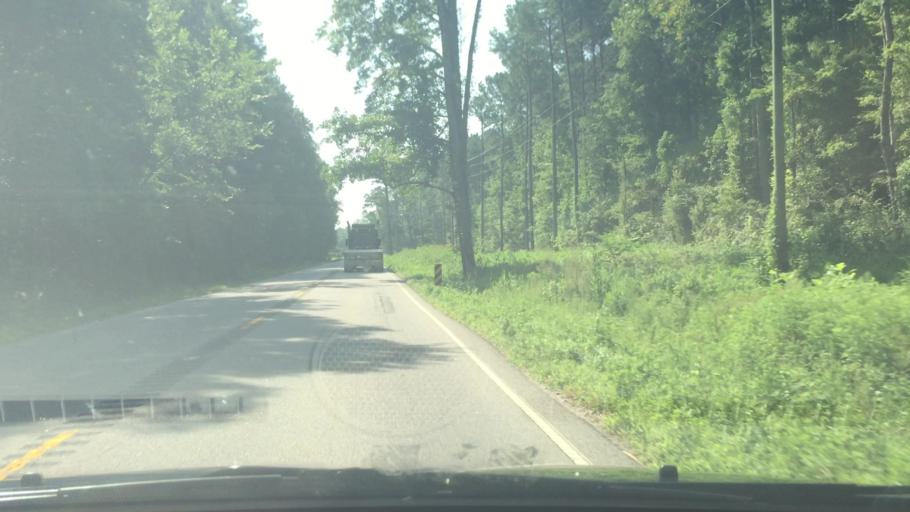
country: US
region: Virginia
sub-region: Sussex County
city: Sussex
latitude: 37.0005
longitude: -77.2645
